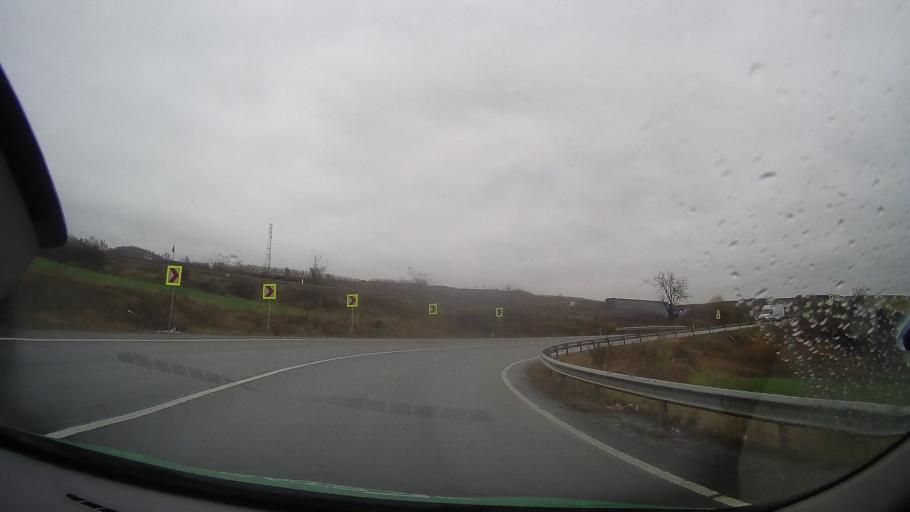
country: RO
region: Bistrita-Nasaud
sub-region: Comuna Teaca
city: Teaca
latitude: 46.9004
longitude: 24.5067
